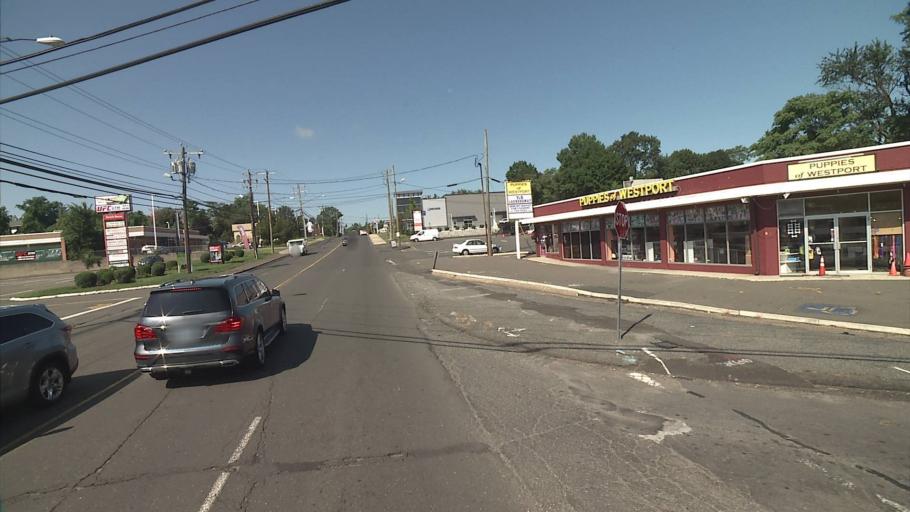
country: US
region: Connecticut
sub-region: Fairfield County
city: Norwalk
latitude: 41.1248
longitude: -73.3963
